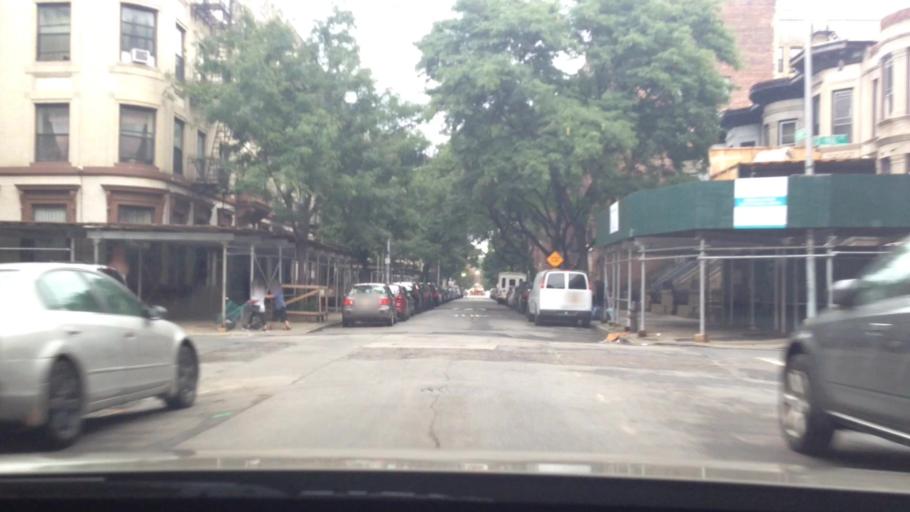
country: US
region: New York
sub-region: Kings County
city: Brooklyn
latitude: 40.6532
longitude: -73.9640
